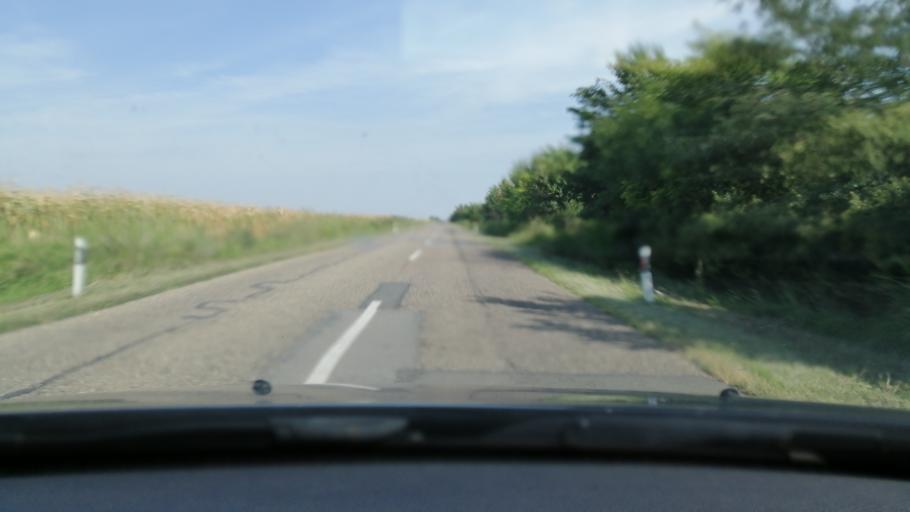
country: RS
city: Uzdin
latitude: 45.1632
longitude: 20.6173
